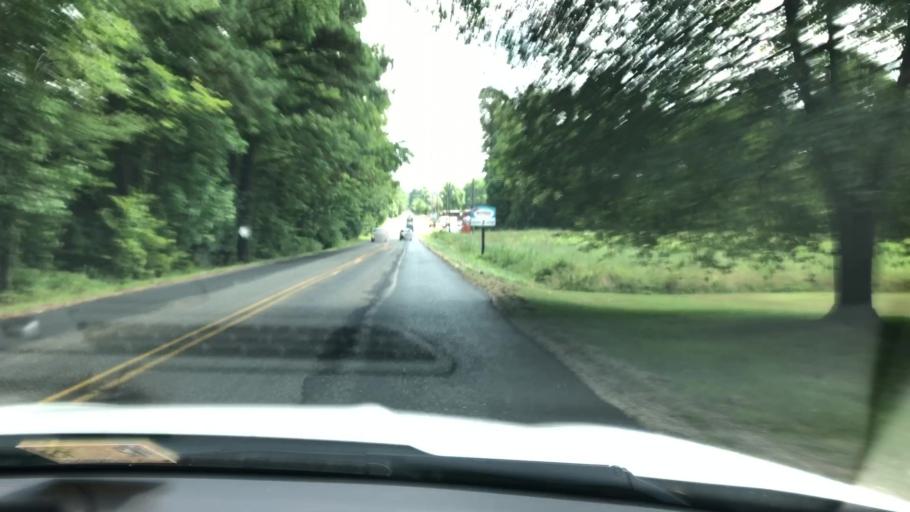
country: US
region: Virginia
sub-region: King William County
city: West Point
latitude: 37.4587
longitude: -76.8415
